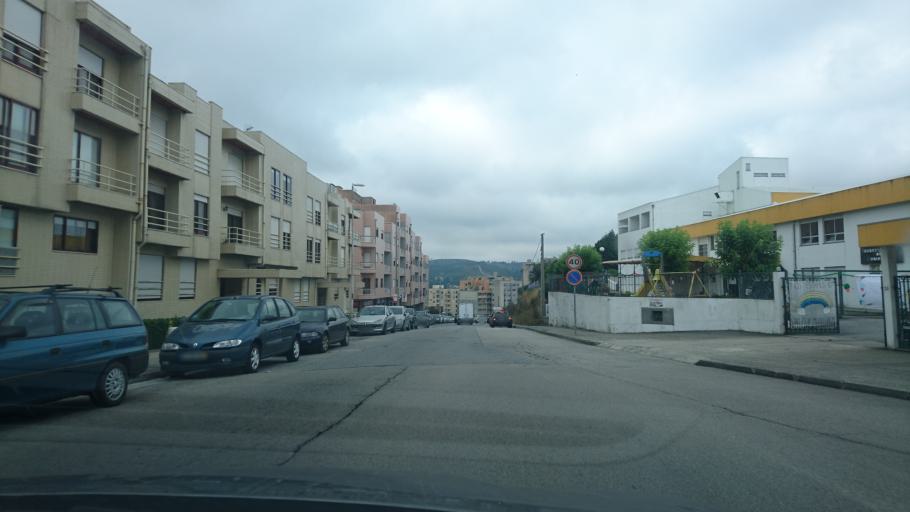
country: PT
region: Porto
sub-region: Valongo
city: Valongo
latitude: 41.1955
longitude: -8.5098
